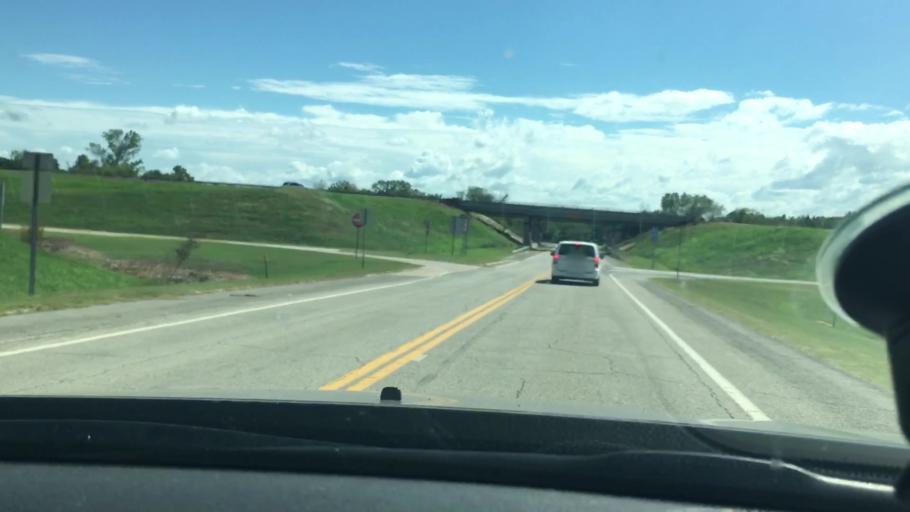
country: US
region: Oklahoma
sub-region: Sequoyah County
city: Vian
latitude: 35.4903
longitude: -94.9723
